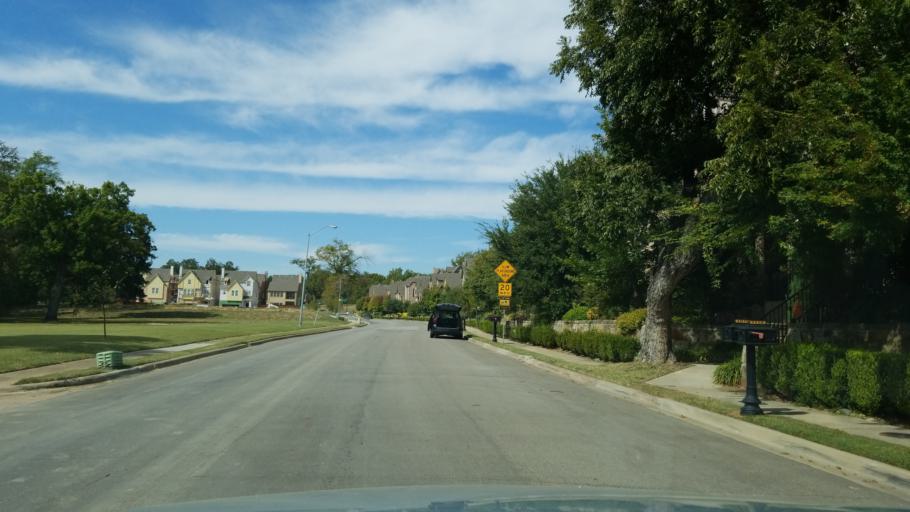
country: US
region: Texas
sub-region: Dallas County
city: Highland Park
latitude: 32.8071
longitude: -96.7346
